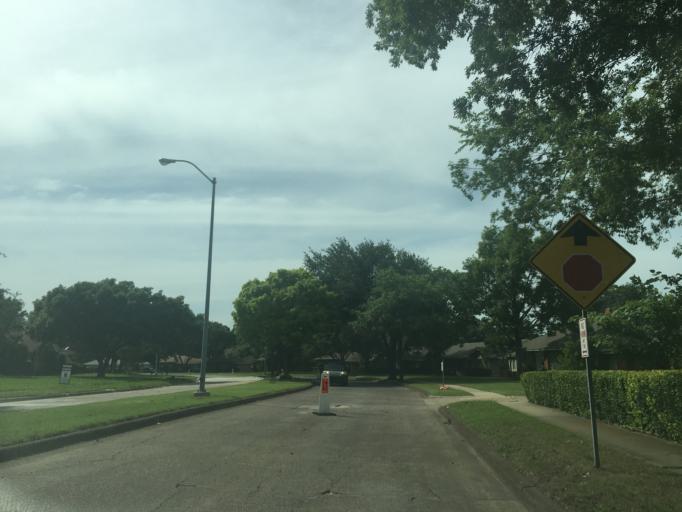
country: US
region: Texas
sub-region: Dallas County
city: Richardson
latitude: 32.9394
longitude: -96.7114
